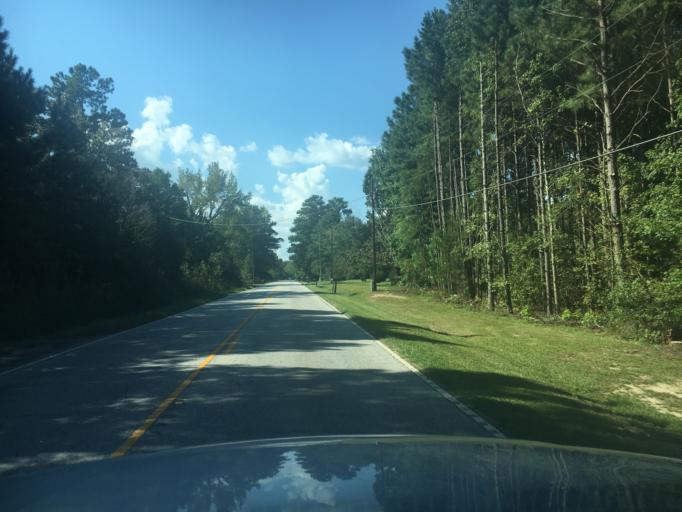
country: US
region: South Carolina
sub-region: Greenwood County
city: Ware Shoals
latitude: 34.2950
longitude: -82.2154
